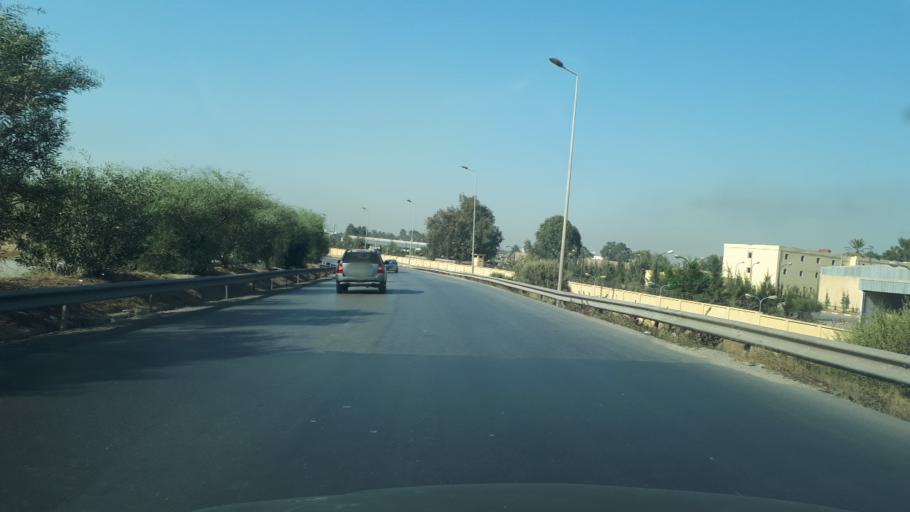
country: DZ
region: Tipaza
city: Baraki
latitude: 36.6824
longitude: 3.0957
